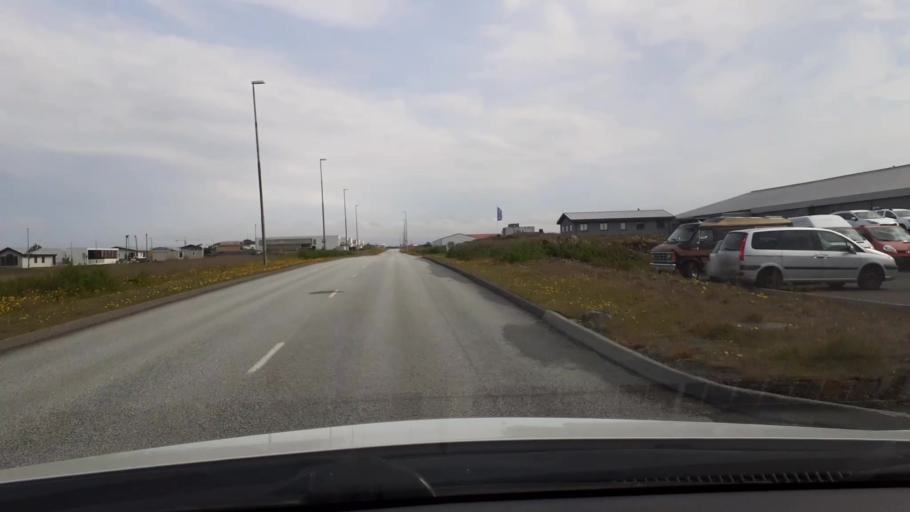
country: IS
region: Southern Peninsula
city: Reykjanesbaer
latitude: 63.9718
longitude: -22.5269
